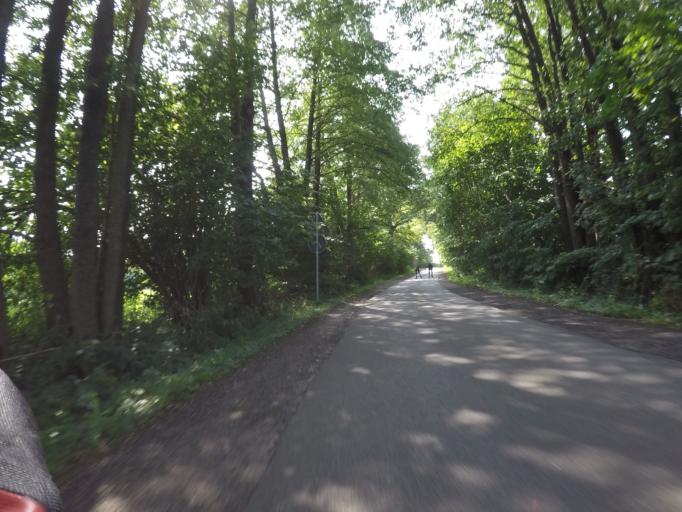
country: DE
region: Schleswig-Holstein
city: Henstedt-Ulzburg
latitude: 53.7679
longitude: 10.0187
